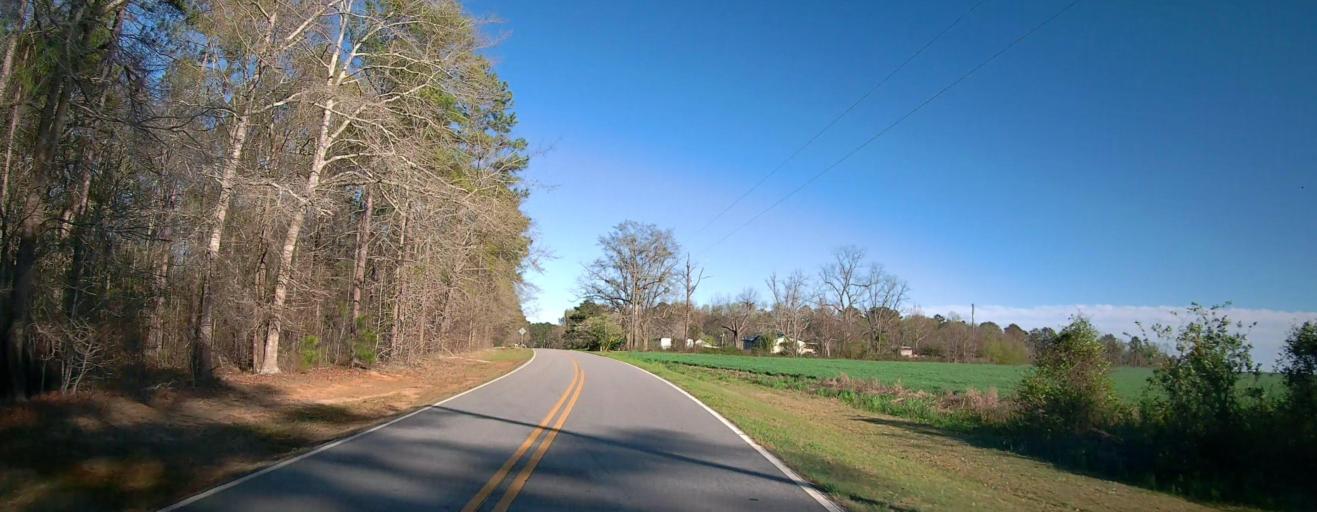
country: US
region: Georgia
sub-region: Houston County
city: Perry
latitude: 32.3615
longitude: -83.6527
